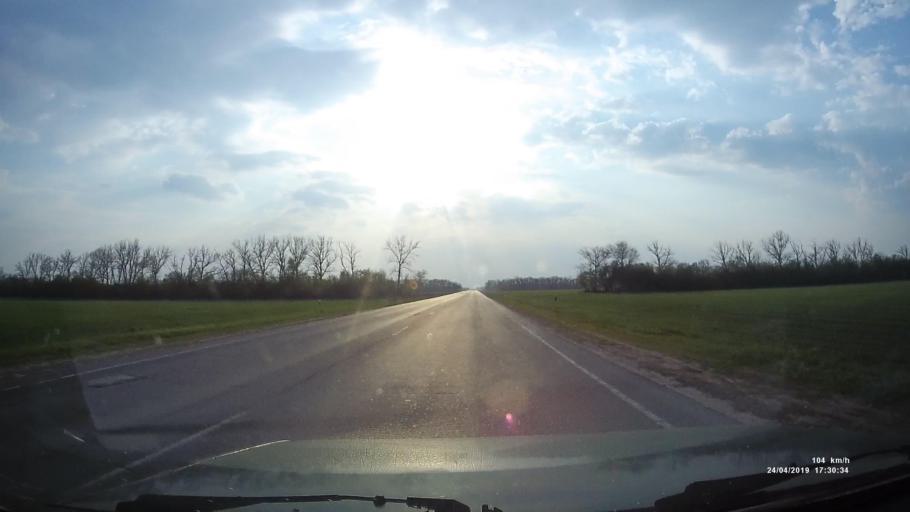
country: RU
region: Rostov
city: Tselina
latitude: 46.5219
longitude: 41.1403
